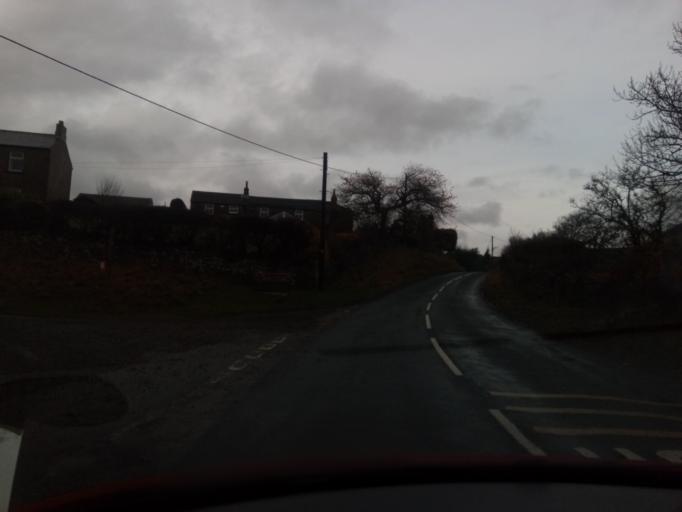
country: GB
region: England
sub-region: County Durham
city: Muggleswick
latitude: 54.8458
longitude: -1.9794
